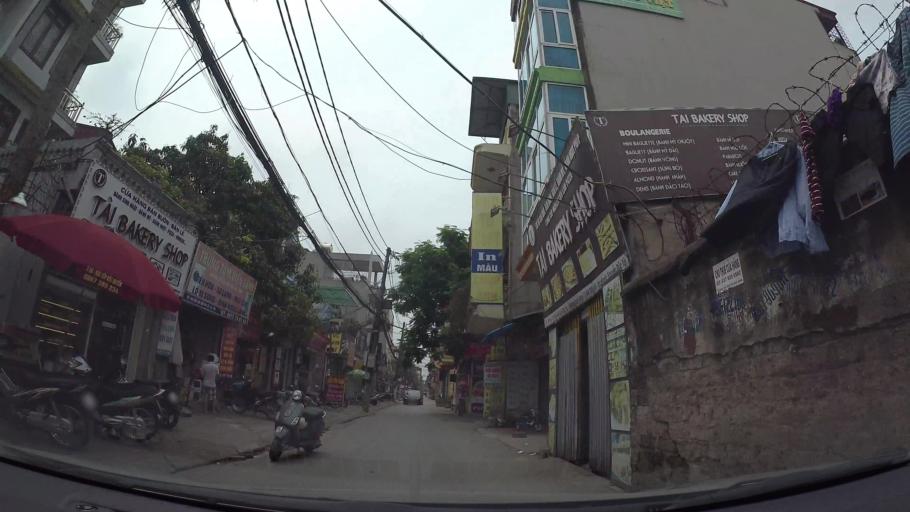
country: VN
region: Ha Noi
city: Trau Quy
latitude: 21.0689
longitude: 105.9074
